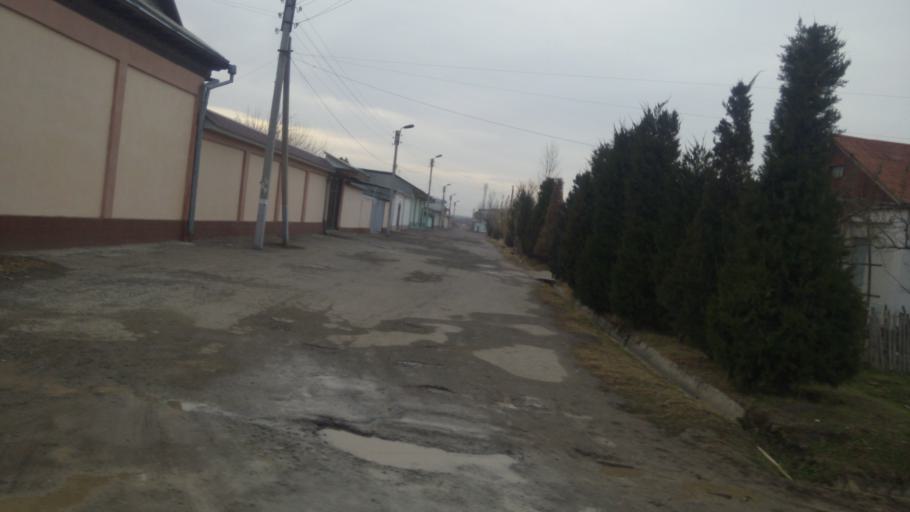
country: UZ
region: Sirdaryo
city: Guliston
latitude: 40.5045
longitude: 68.7803
